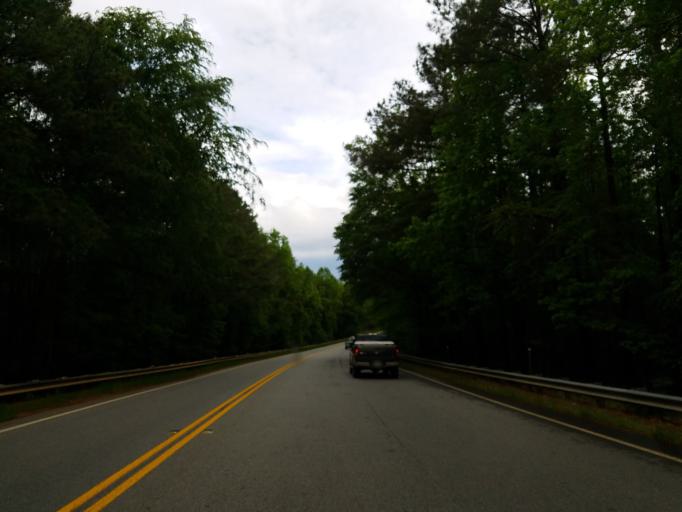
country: US
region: Georgia
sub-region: Crawford County
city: Roberta
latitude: 32.8205
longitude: -84.0556
